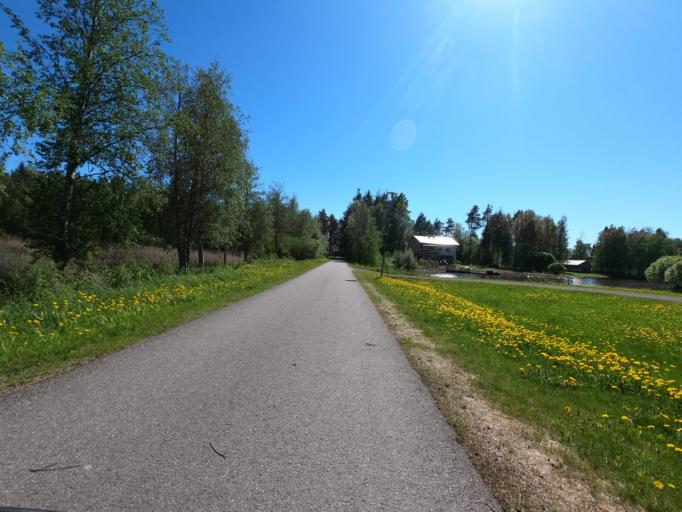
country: FI
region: North Karelia
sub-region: Joensuu
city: Joensuu
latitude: 62.5794
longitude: 29.7664
